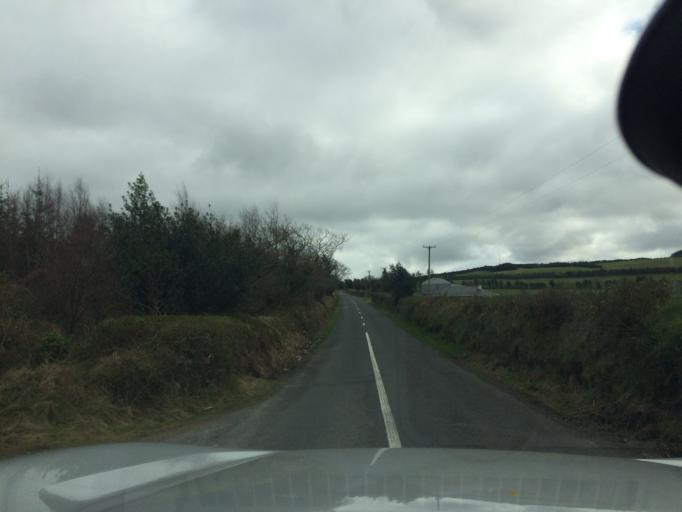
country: IE
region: Munster
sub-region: South Tipperary
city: Cluain Meala
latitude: 52.3409
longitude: -7.6309
